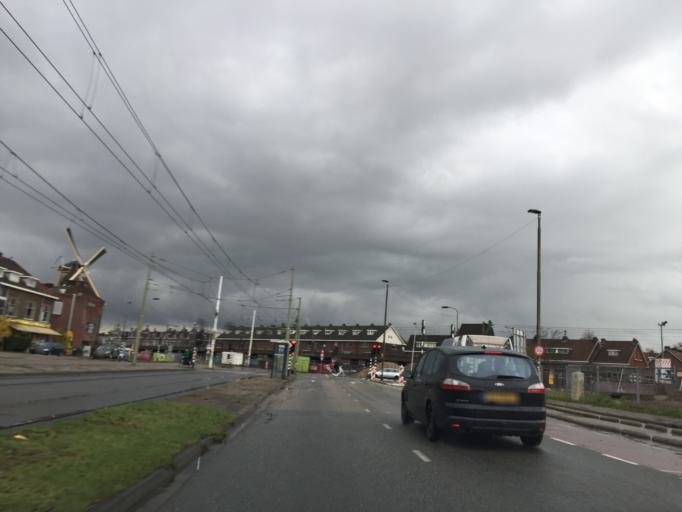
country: NL
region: South Holland
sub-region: Gemeente Delft
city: Delft
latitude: 52.0157
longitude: 4.3508
